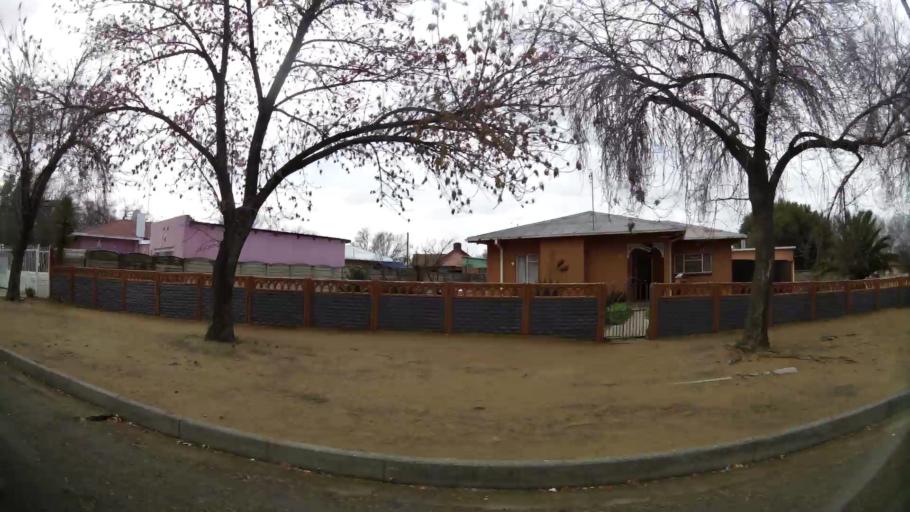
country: ZA
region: Orange Free State
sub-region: Fezile Dabi District Municipality
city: Kroonstad
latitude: -27.6327
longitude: 27.2280
